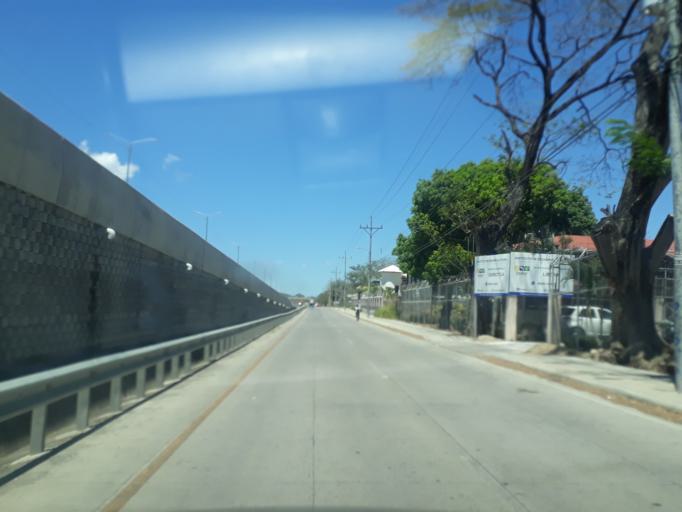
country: CR
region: Guanacaste
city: Liberia
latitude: 10.6324
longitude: -85.4472
